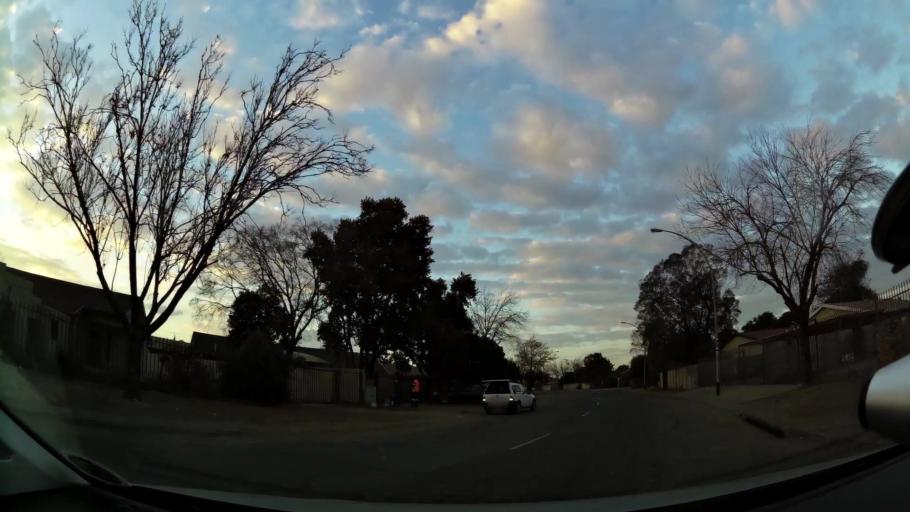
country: ZA
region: Orange Free State
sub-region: Mangaung Metropolitan Municipality
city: Bloemfontein
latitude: -29.1734
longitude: 26.1908
